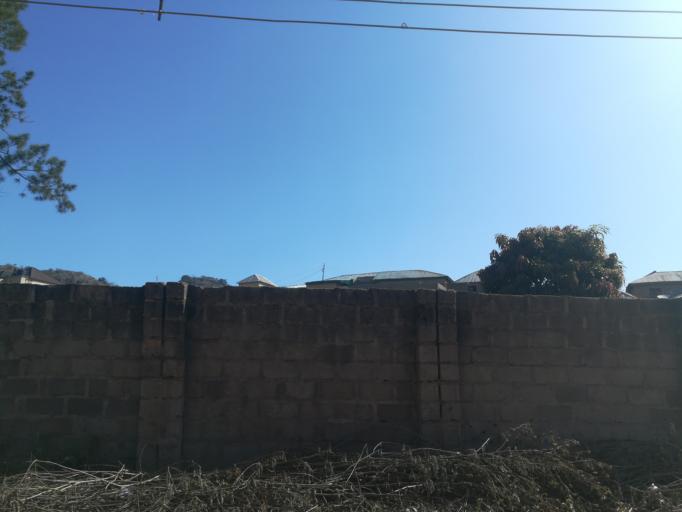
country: NG
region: Plateau
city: Jos
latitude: 9.9368
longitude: 8.8985
